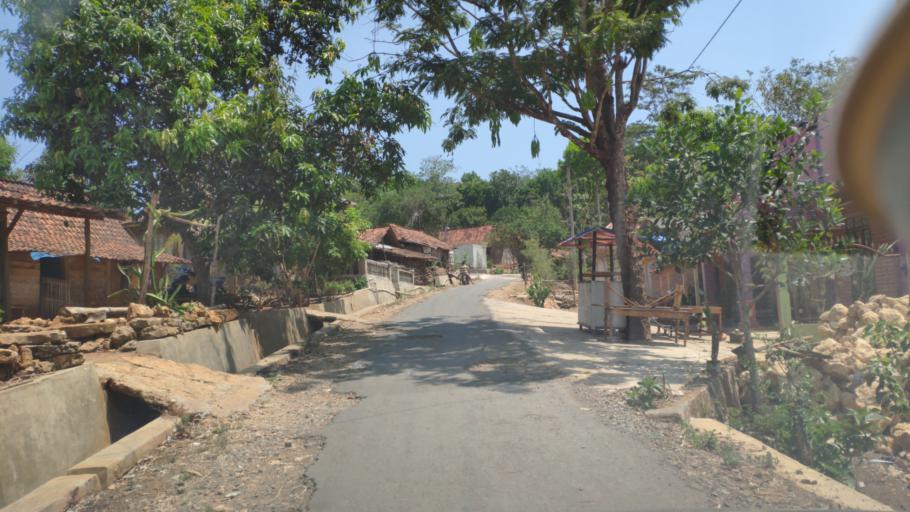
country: ID
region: Central Java
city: Guyangan
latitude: -6.9337
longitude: 111.1222
